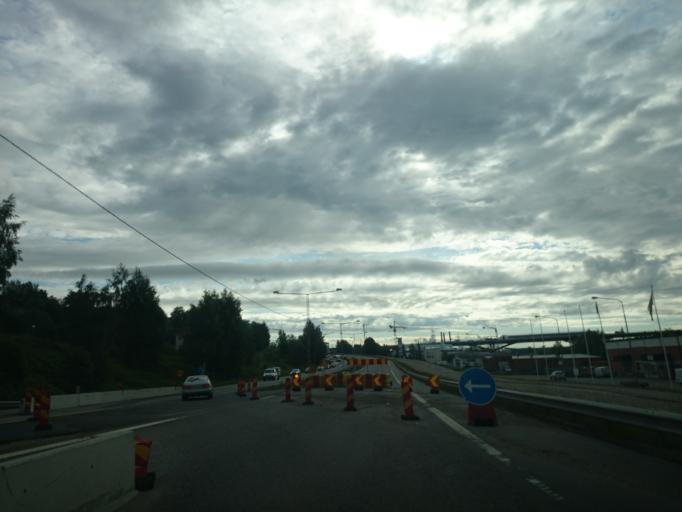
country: SE
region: Vaesternorrland
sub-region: Sundsvalls Kommun
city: Sundsvall
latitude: 62.3950
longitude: 17.3253
